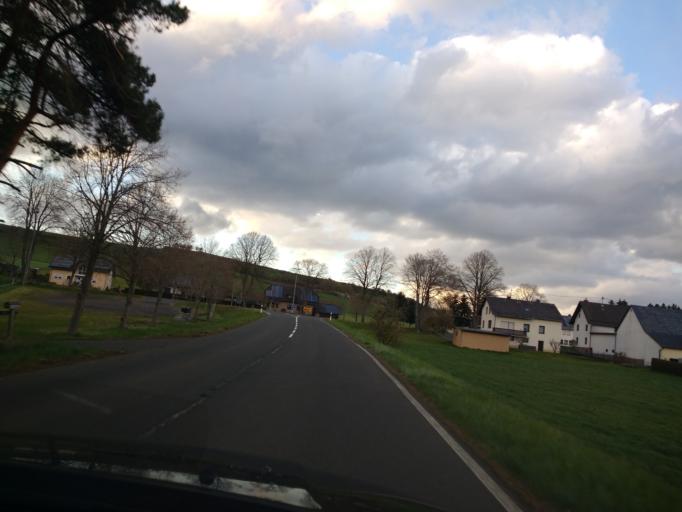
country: DE
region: Rheinland-Pfalz
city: Steffeln
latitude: 50.2865
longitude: 6.5718
